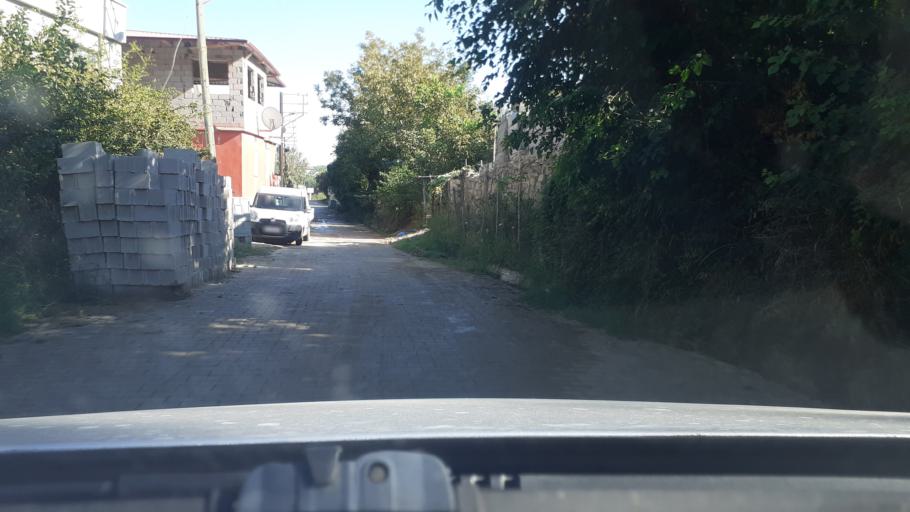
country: TR
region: Hatay
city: Kirikhan
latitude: 36.4877
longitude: 36.3011
